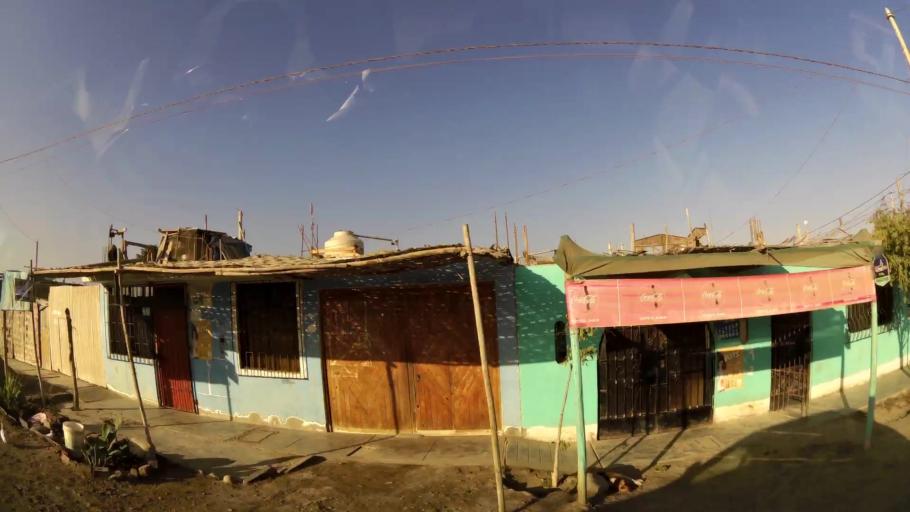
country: PE
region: Ica
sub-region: Provincia de Pisco
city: Villa Tupac Amaru
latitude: -13.7088
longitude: -76.1457
